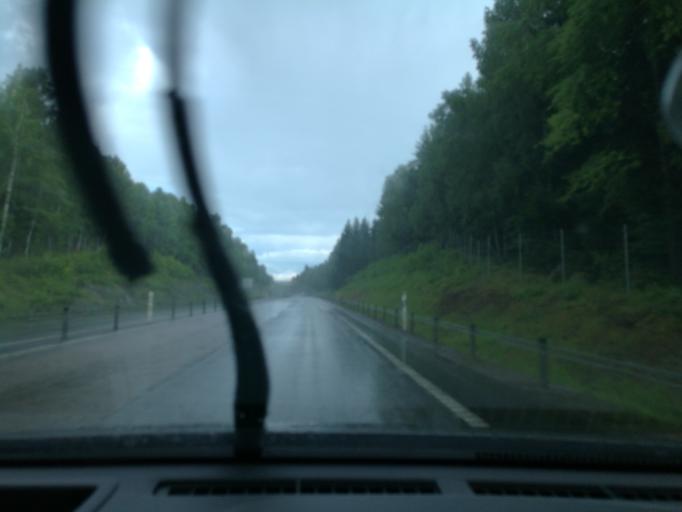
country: SE
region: Vaestmanland
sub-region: Vasteras
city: Skultuna
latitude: 59.6366
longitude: 16.4306
